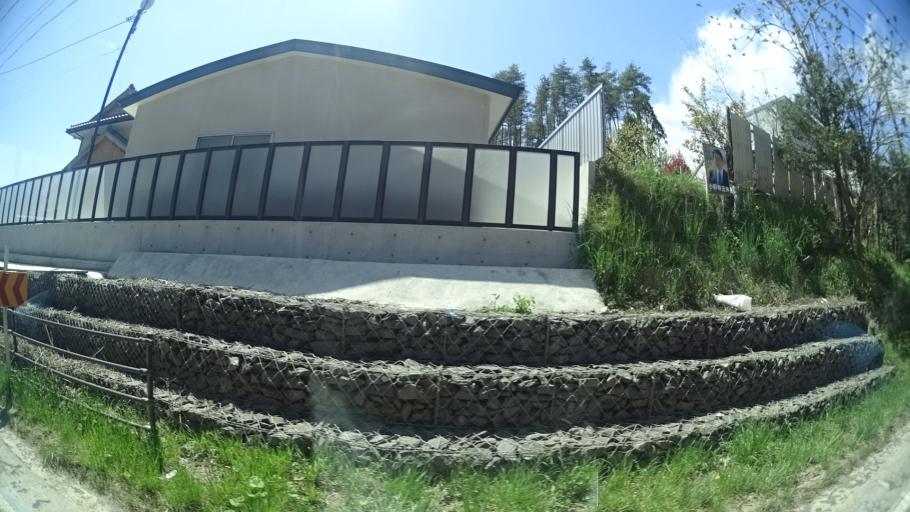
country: JP
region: Miyagi
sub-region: Oshika Gun
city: Onagawa Cho
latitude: 38.7106
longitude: 141.5100
